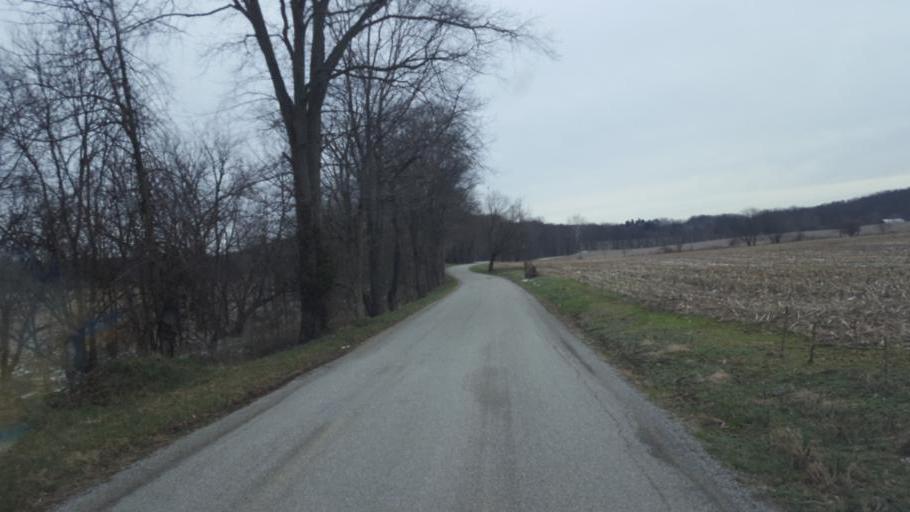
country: US
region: Ohio
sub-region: Sandusky County
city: Bellville
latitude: 40.5963
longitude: -82.4598
